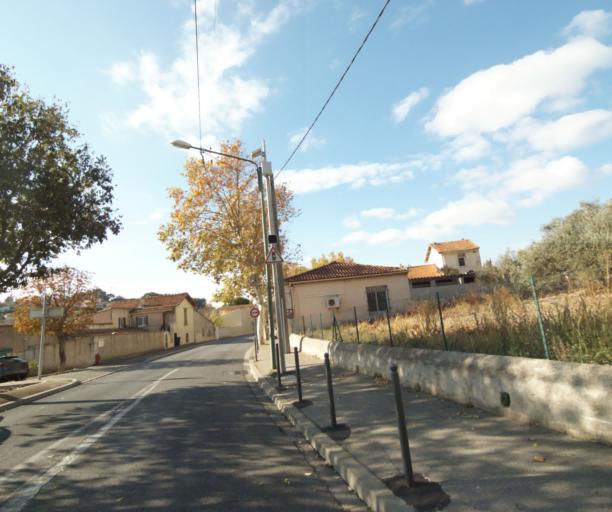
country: FR
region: Provence-Alpes-Cote d'Azur
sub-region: Departement des Bouches-du-Rhone
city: Allauch
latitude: 43.3532
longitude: 5.4837
